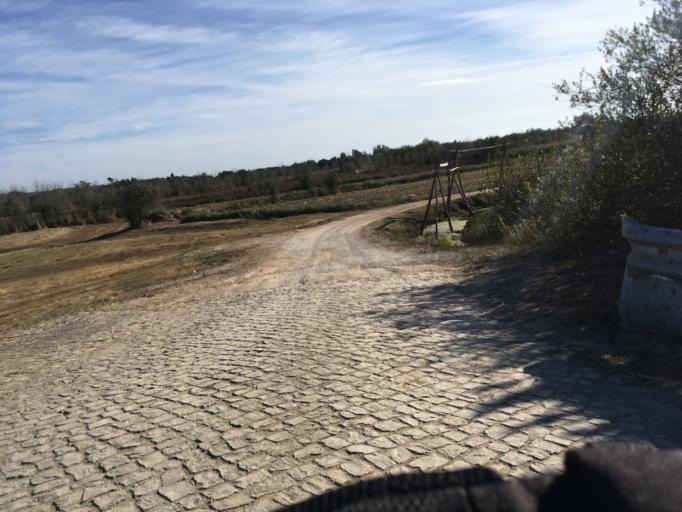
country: PT
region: Aveiro
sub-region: Estarreja
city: Salreu
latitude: 40.7308
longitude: -8.5672
